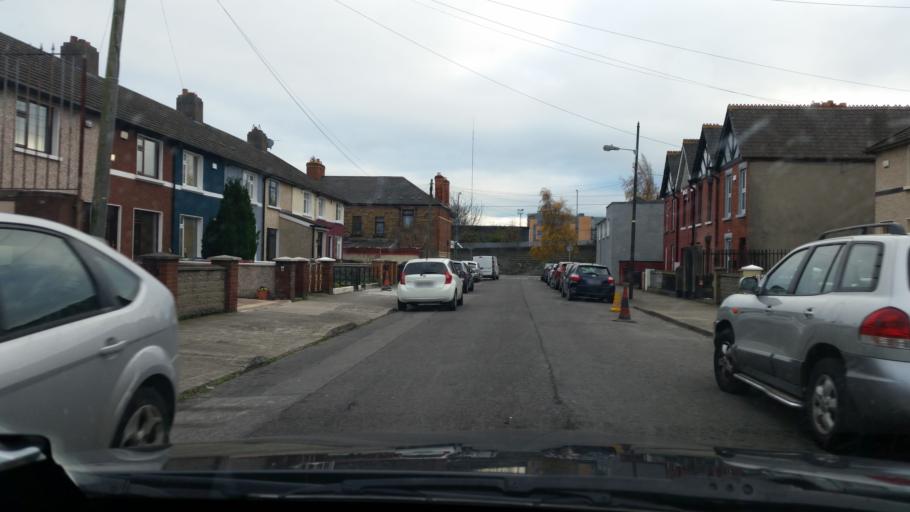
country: IE
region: Leinster
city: Ringsend
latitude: 53.3527
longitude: -6.2337
